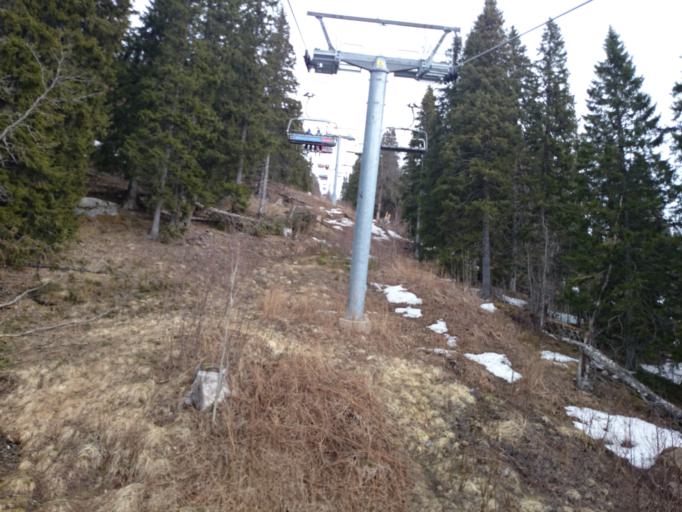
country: SE
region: Jaemtland
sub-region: Are Kommun
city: Are
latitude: 63.4049
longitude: 13.0808
